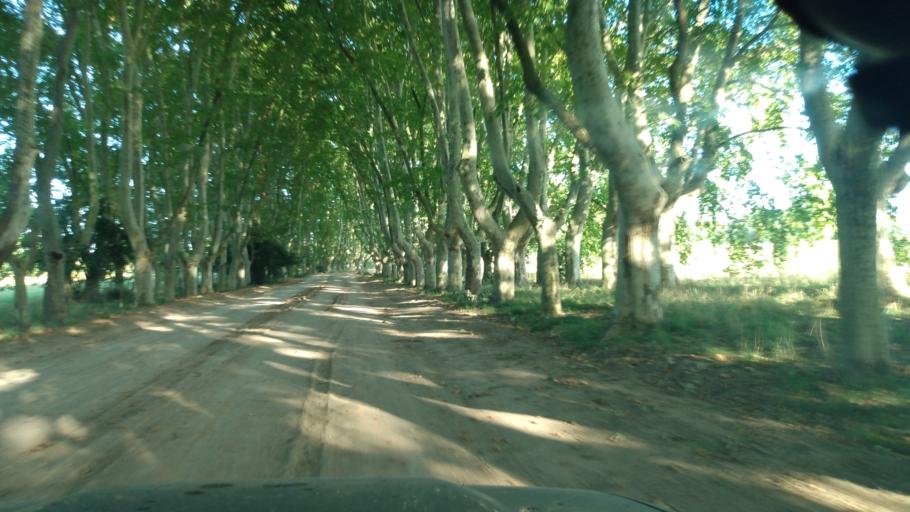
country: AR
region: Buenos Aires
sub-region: Partido de Lujan
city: Lujan
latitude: -34.5812
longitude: -59.0833
